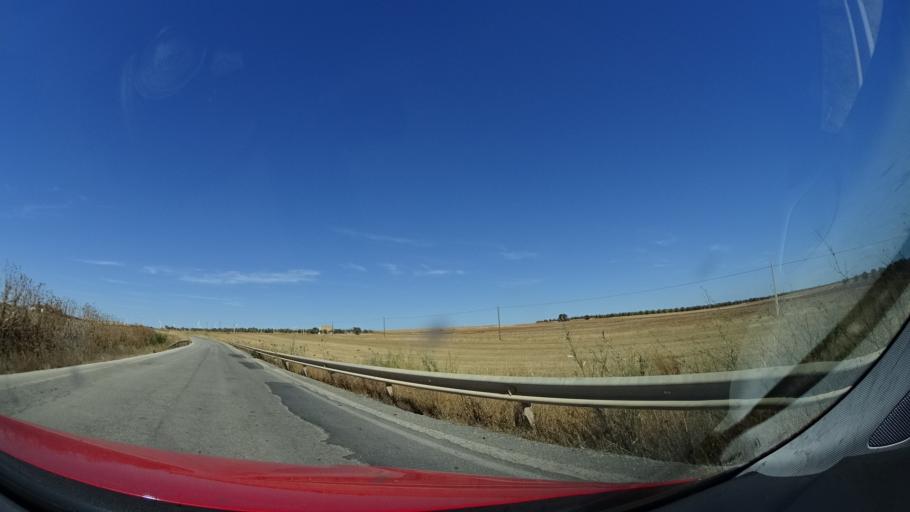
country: ES
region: Andalusia
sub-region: Provincia de Malaga
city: Campillos
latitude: 37.0707
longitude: -4.8621
